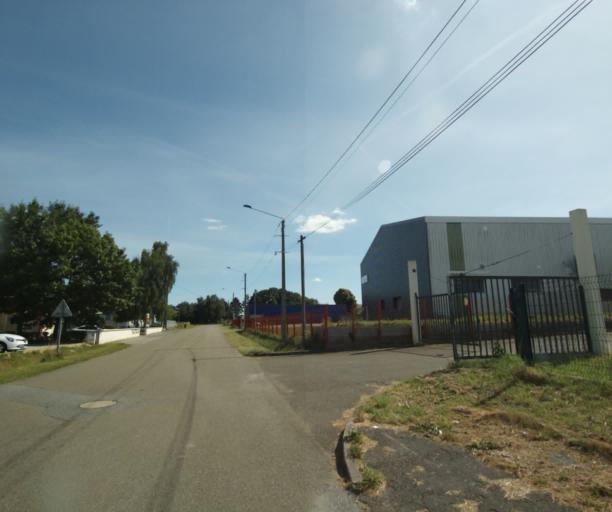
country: FR
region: Pays de la Loire
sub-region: Departement de la Mayenne
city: Change
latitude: 48.0724
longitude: -0.7981
